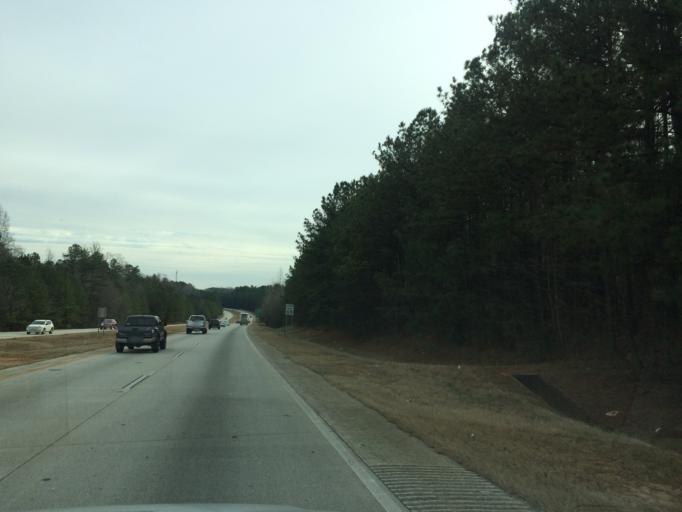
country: US
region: Georgia
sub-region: Gwinnett County
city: Dacula
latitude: 33.9812
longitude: -83.9245
